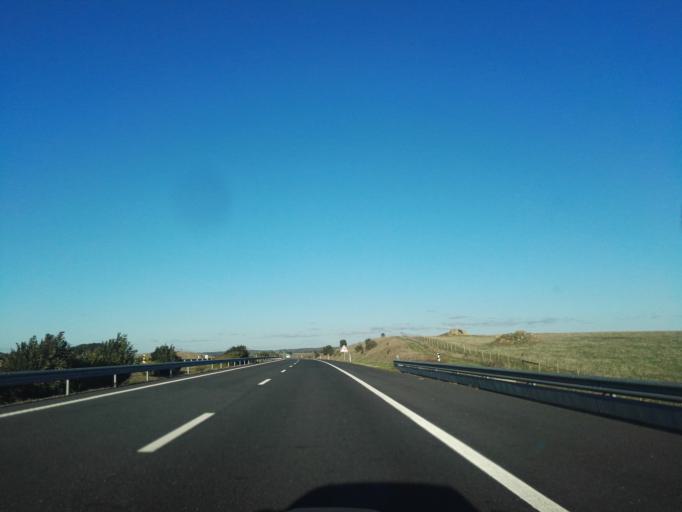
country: PT
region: Evora
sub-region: Evora
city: Evora
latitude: 38.6516
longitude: -7.8499
